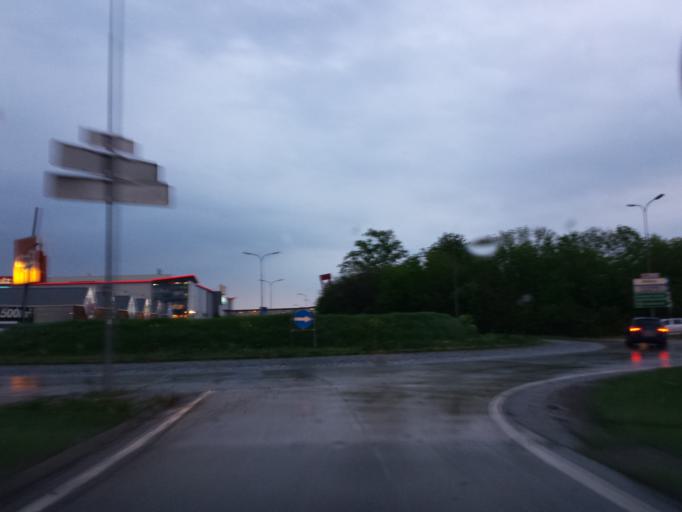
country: AT
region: Lower Austria
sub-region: Politischer Bezirk Modling
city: Wiener Neudorf
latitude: 48.1047
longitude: 16.3103
